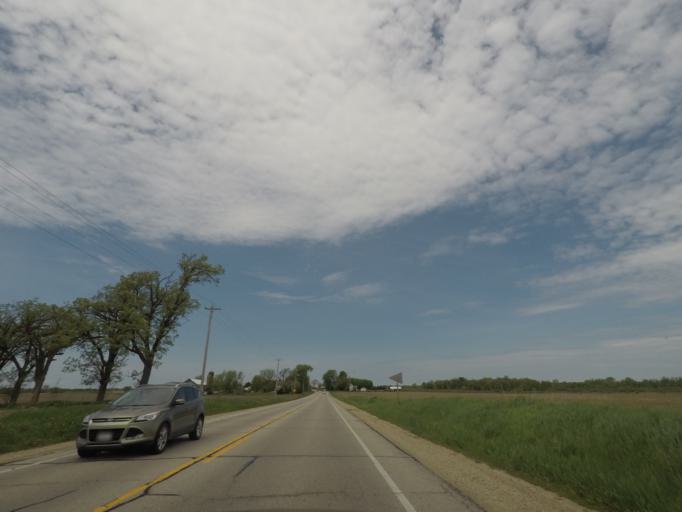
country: US
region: Wisconsin
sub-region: Green County
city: Brooklyn
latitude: 42.8421
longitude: -89.3263
